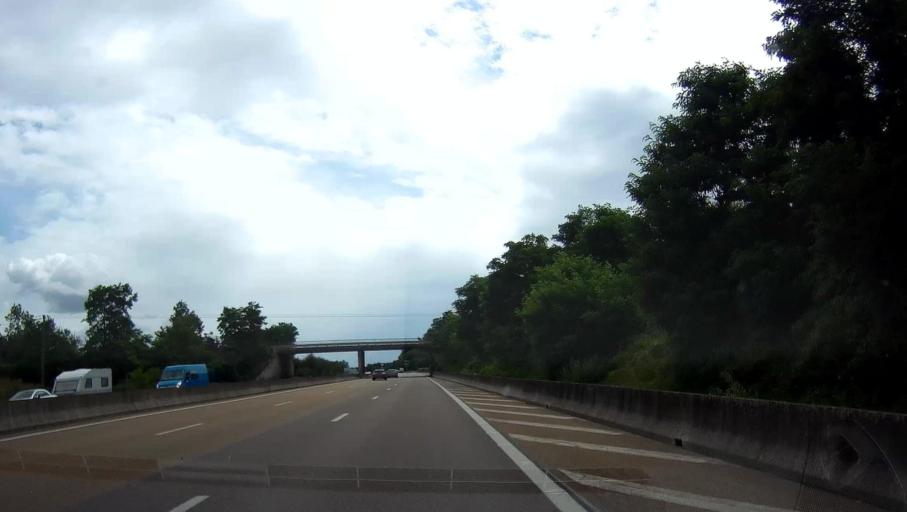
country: FR
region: Bourgogne
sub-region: Departement de la Cote-d'Or
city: Arc-sur-Tille
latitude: 47.3631
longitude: 5.1633
